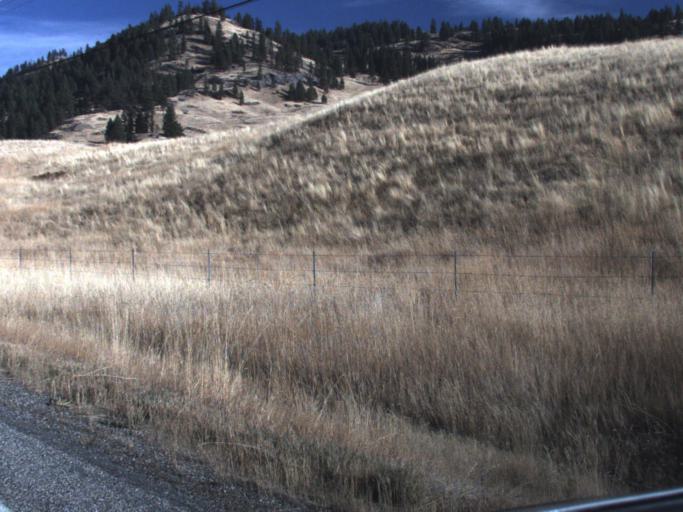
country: US
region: Washington
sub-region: Ferry County
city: Republic
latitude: 48.7134
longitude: -118.6553
